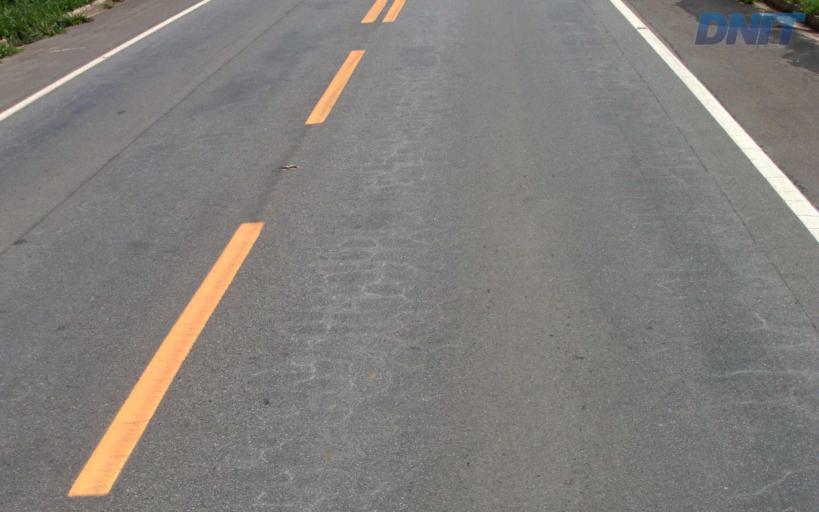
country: BR
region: Minas Gerais
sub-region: Belo Oriente
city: Belo Oriente
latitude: -19.0860
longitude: -42.1873
